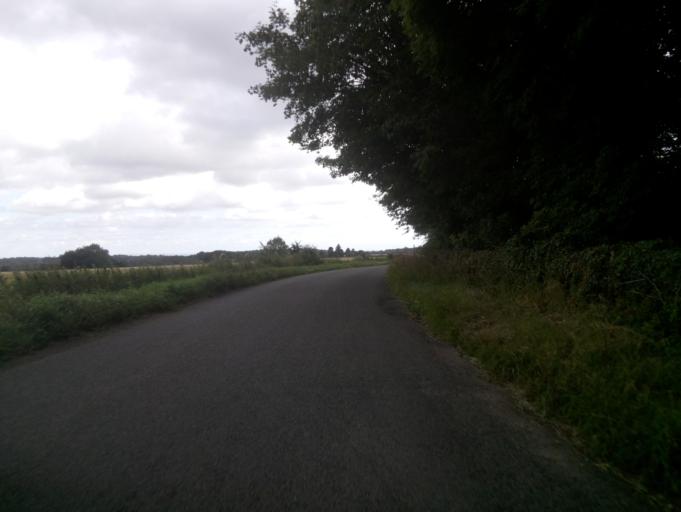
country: GB
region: England
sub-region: Gloucestershire
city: Chalford
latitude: 51.7714
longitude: -2.0912
